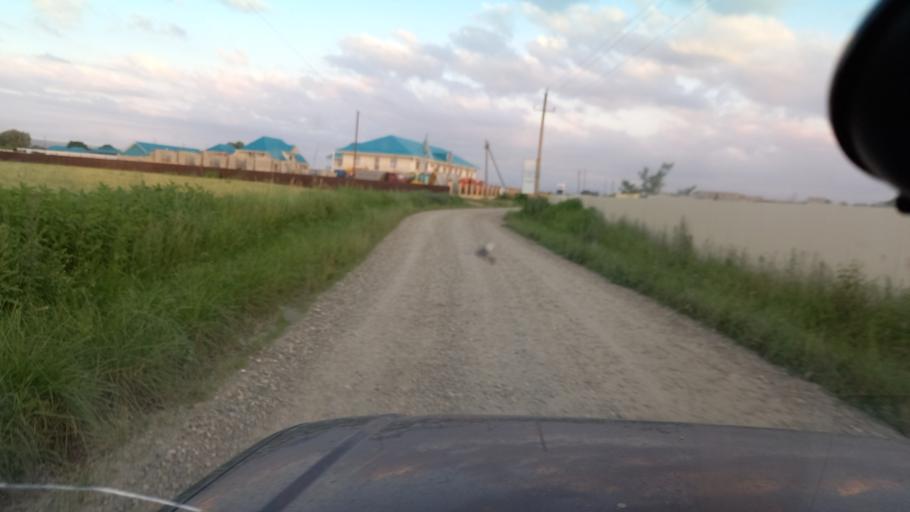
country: RU
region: Krasnodarskiy
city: Mostovskoy
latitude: 44.4381
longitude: 40.7418
